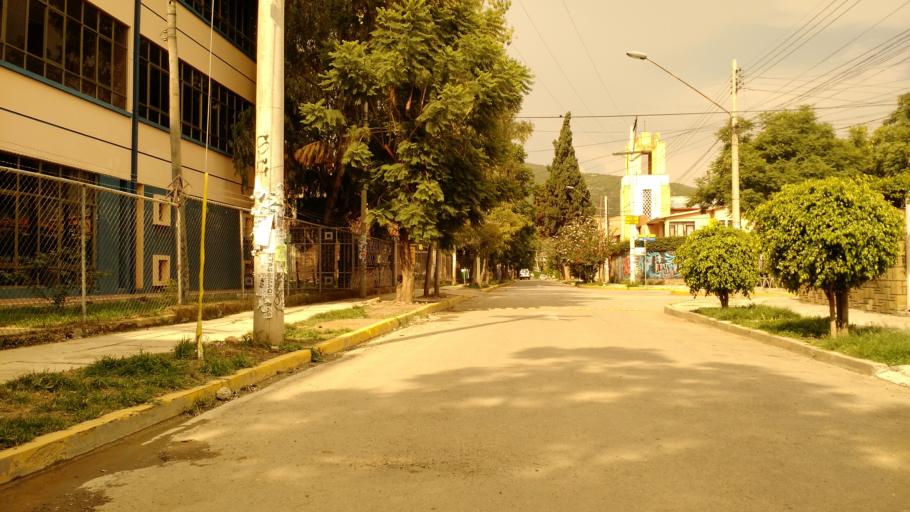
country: BO
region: Cochabamba
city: Cochabamba
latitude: -17.3952
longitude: -66.1463
